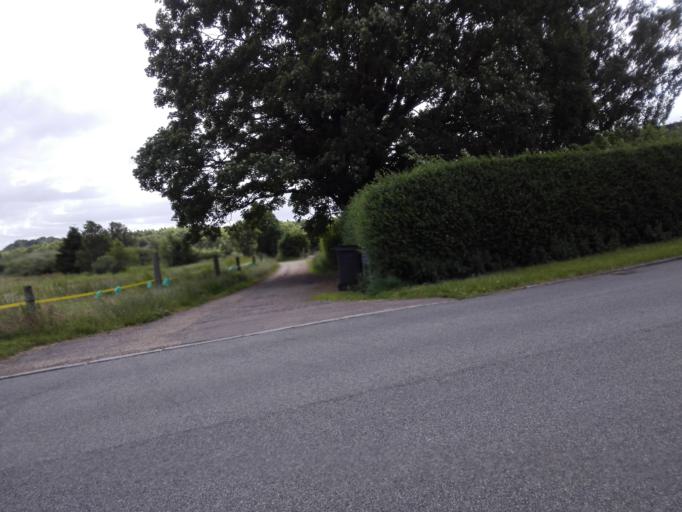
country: DK
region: Capital Region
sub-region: Frederikssund Kommune
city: Slangerup
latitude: 55.8415
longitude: 12.1861
